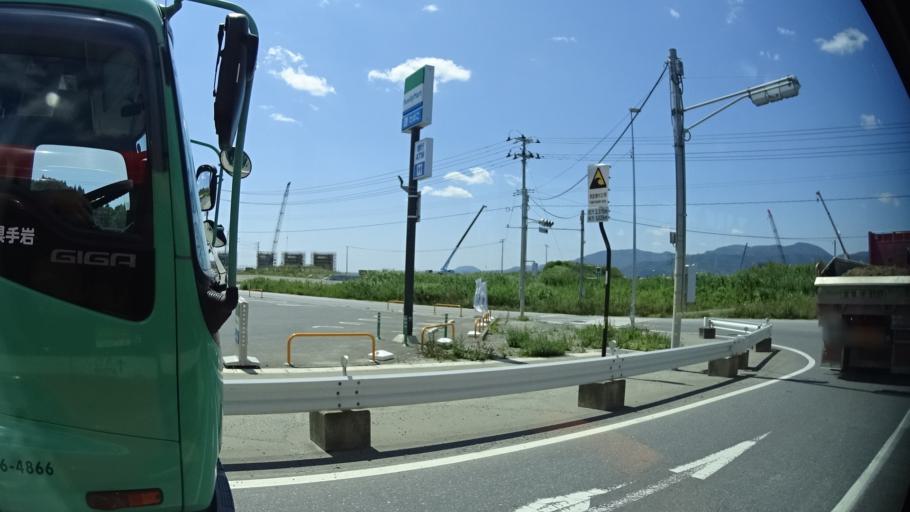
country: JP
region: Iwate
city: Ofunato
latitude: 39.0088
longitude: 141.6504
